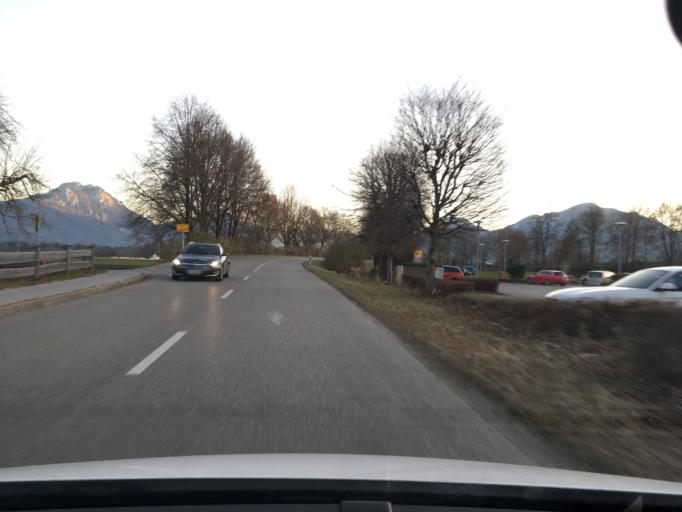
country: DE
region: Bavaria
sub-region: Upper Bavaria
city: Raubling
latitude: 47.7754
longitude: 12.1058
